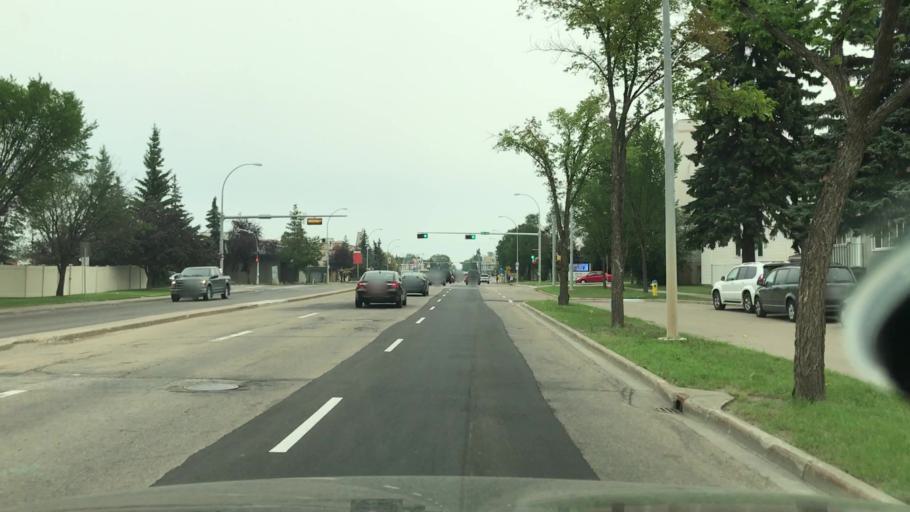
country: CA
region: Alberta
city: Edmonton
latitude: 53.5384
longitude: -113.5779
